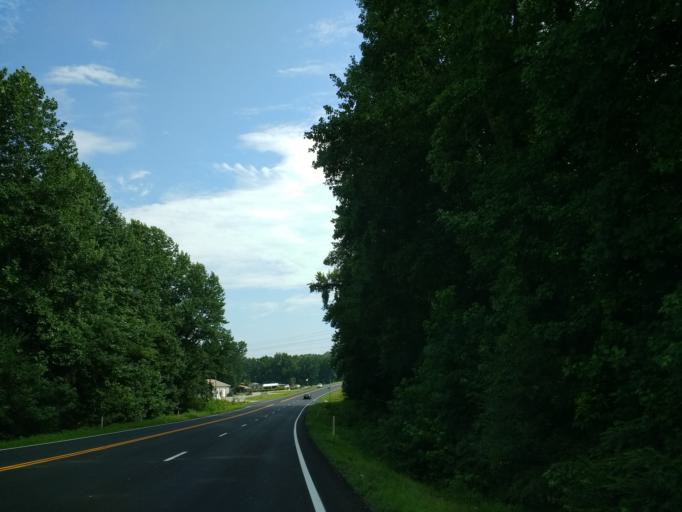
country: US
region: Georgia
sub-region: White County
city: Cleveland
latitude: 34.4969
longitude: -83.7560
